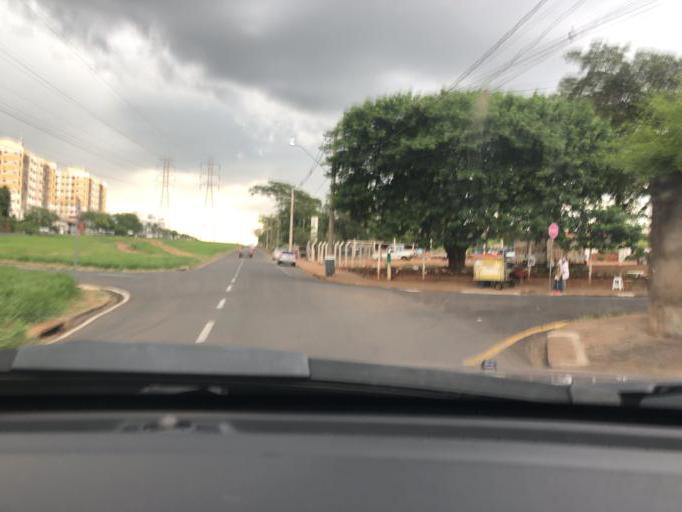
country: BR
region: Sao Paulo
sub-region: Sao Jose Do Rio Preto
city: Sao Jose do Rio Preto
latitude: -20.8440
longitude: -49.3839
